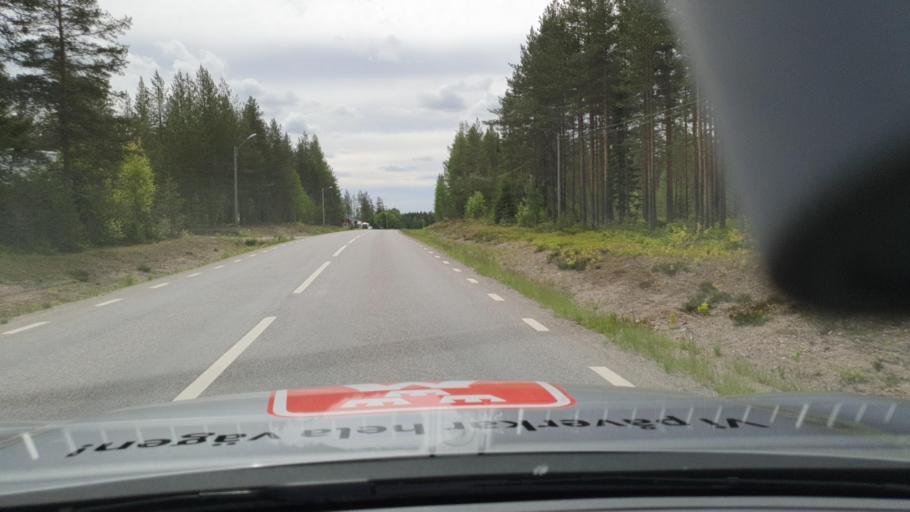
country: SE
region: Norrbotten
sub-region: Kalix Kommun
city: Kalix
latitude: 65.9530
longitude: 23.4534
